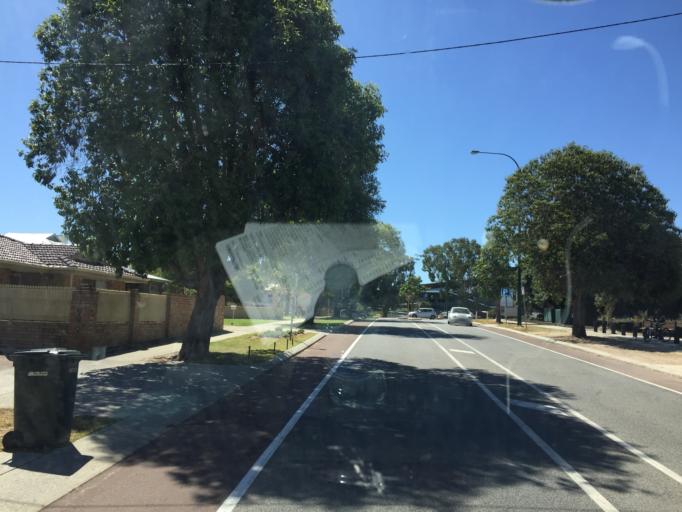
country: AU
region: Western Australia
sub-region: Victoria Park
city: Victoria Park
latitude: -31.9751
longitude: 115.9092
